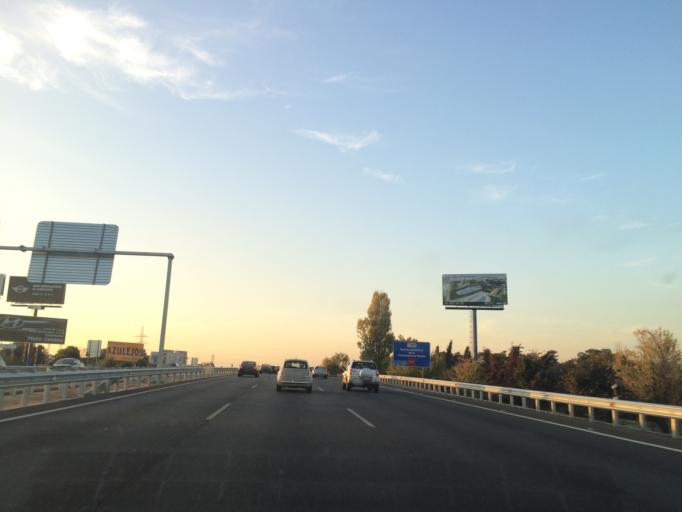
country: ES
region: Madrid
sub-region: Provincia de Madrid
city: Pozuelo de Alarcon
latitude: 40.4356
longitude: -3.8416
